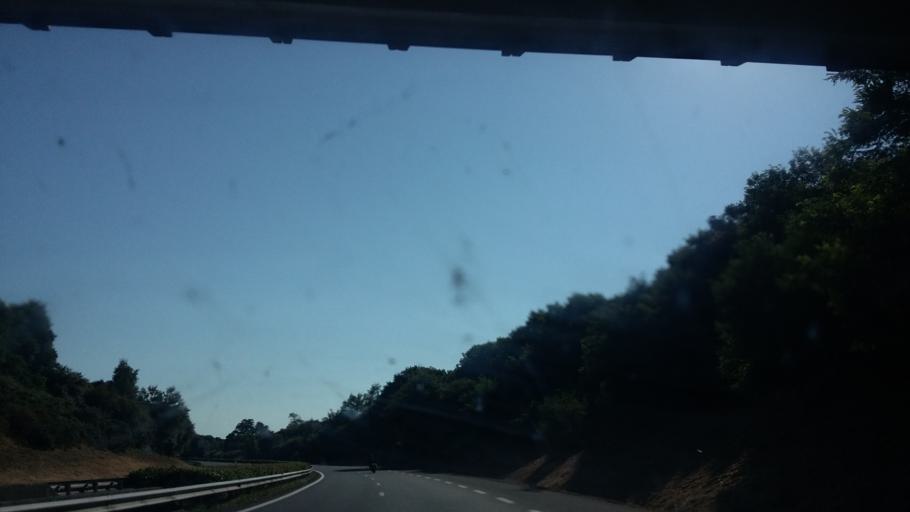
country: FR
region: Pays de la Loire
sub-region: Departement de la Vendee
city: Challans
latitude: 46.8622
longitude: -1.8744
